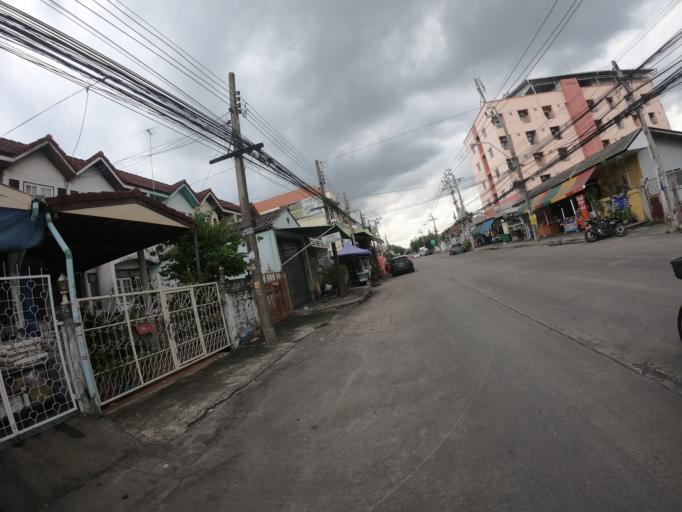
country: TH
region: Bangkok
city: Suan Luang
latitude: 13.7124
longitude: 100.6590
